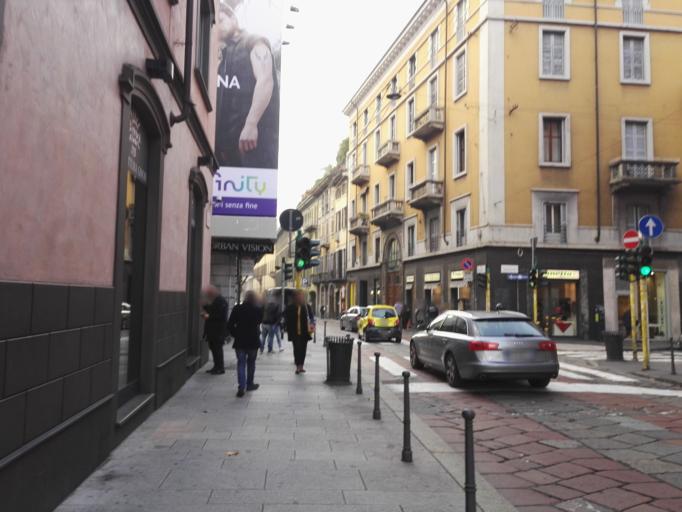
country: IT
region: Lombardy
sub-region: Citta metropolitana di Milano
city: Milano
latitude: 45.4729
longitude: 9.1877
